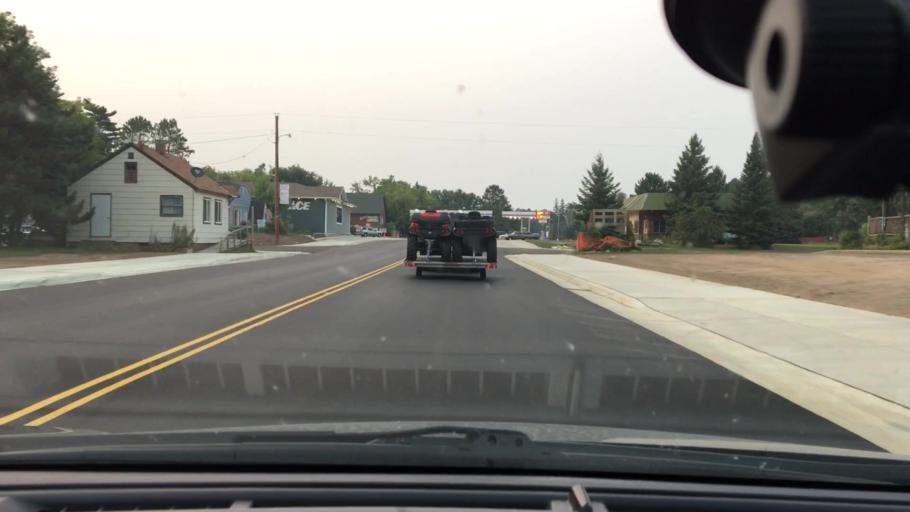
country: US
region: Minnesota
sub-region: Crow Wing County
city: Cross Lake
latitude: 46.7294
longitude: -93.9583
